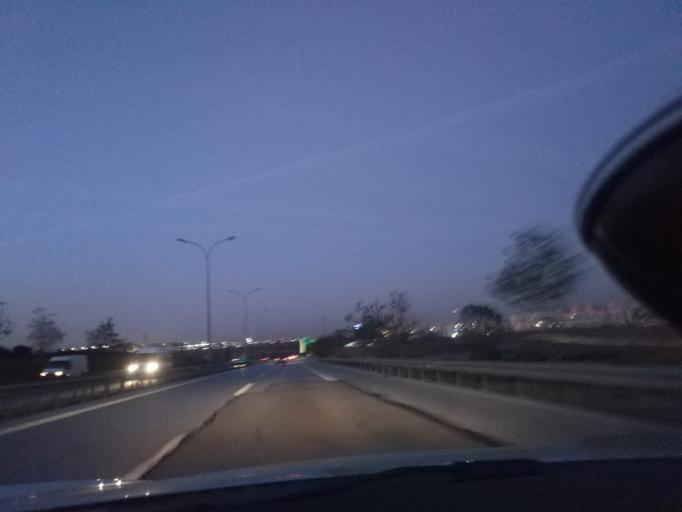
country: TR
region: Istanbul
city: Sultanbeyli
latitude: 40.9241
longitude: 29.3240
